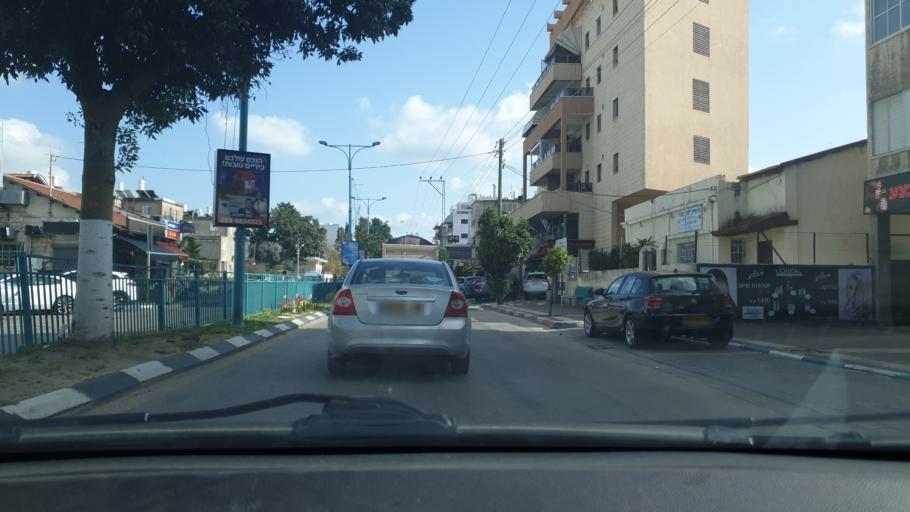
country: IL
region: Central District
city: Ramla
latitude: 31.9347
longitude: 34.8674
